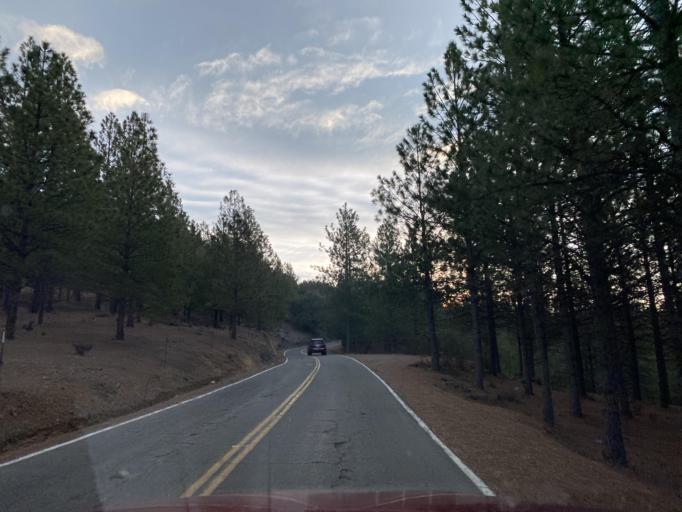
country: US
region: California
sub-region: Amador County
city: Pioneer
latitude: 38.4980
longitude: -120.5996
